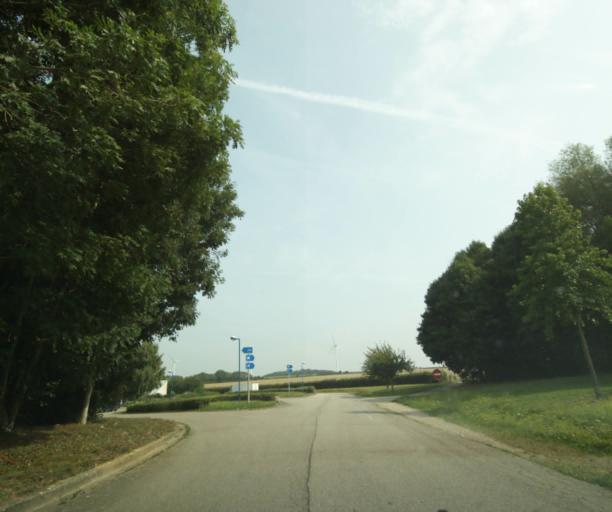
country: FR
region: Lower Normandy
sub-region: Departement du Calvados
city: Falaise
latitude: 48.9349
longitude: -0.2080
